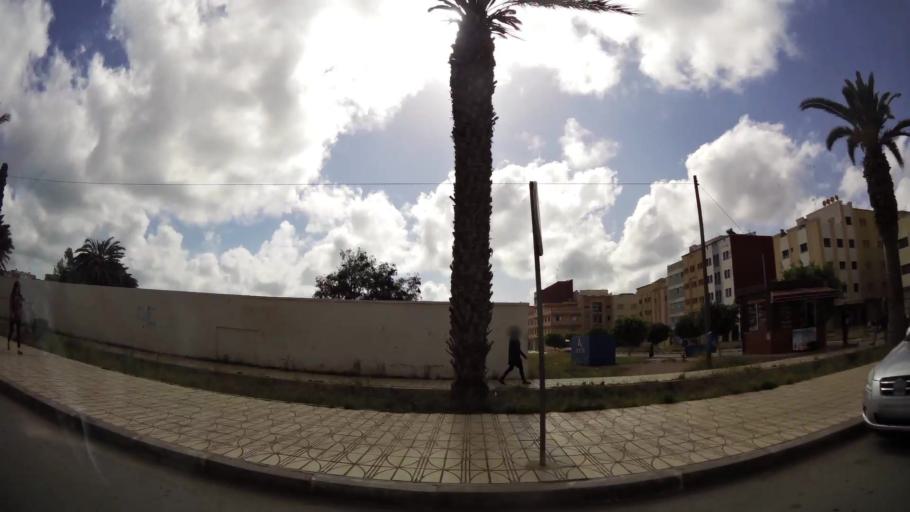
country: MA
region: Oriental
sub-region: Nador
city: Nador
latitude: 35.1710
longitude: -2.9245
